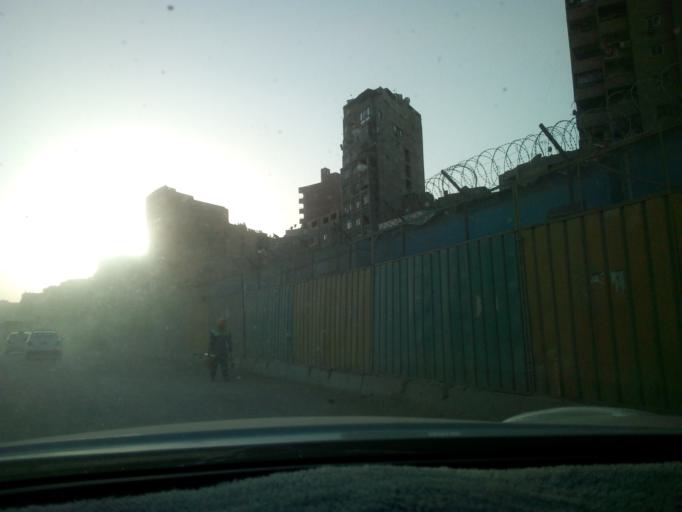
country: EG
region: Muhafazat al Qalyubiyah
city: Al Khankah
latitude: 30.1259
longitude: 31.3501
